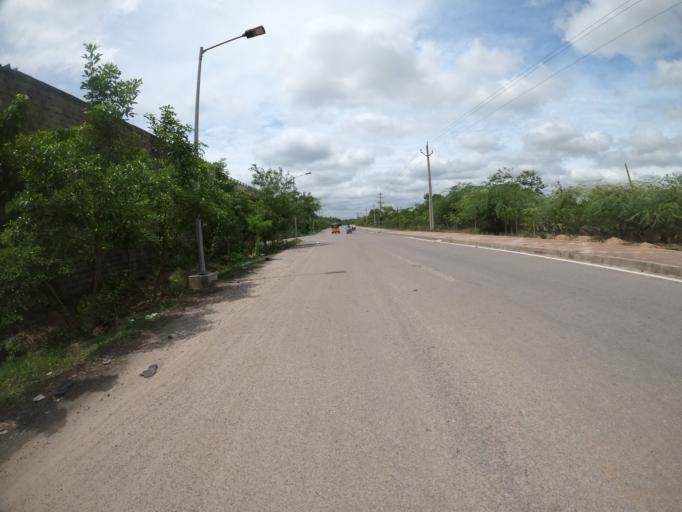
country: IN
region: Telangana
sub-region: Rangareddi
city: Balapur
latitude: 17.2827
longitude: 78.3825
